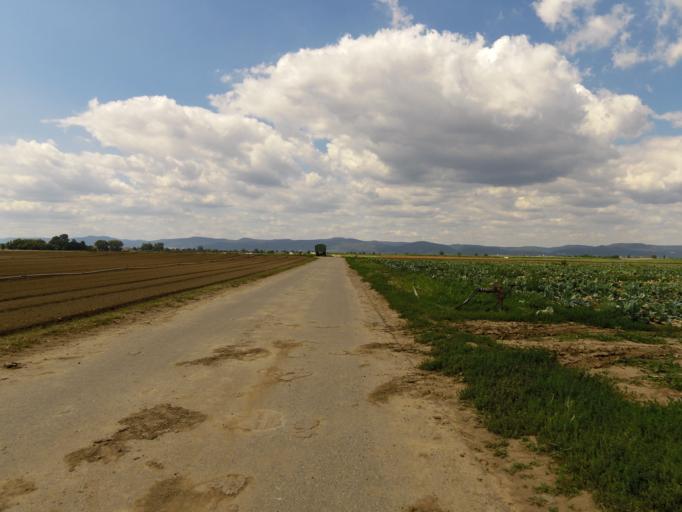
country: DE
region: Rheinland-Pfalz
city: Dannstadt-Schauernheim
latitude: 49.4416
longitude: 8.2933
